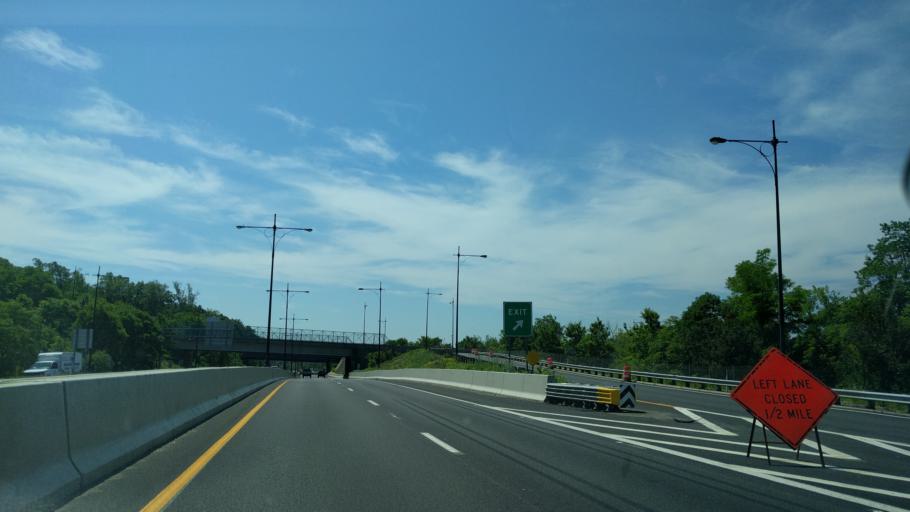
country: US
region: Massachusetts
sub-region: Worcester County
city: Millbury
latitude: 42.2130
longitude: -71.7828
